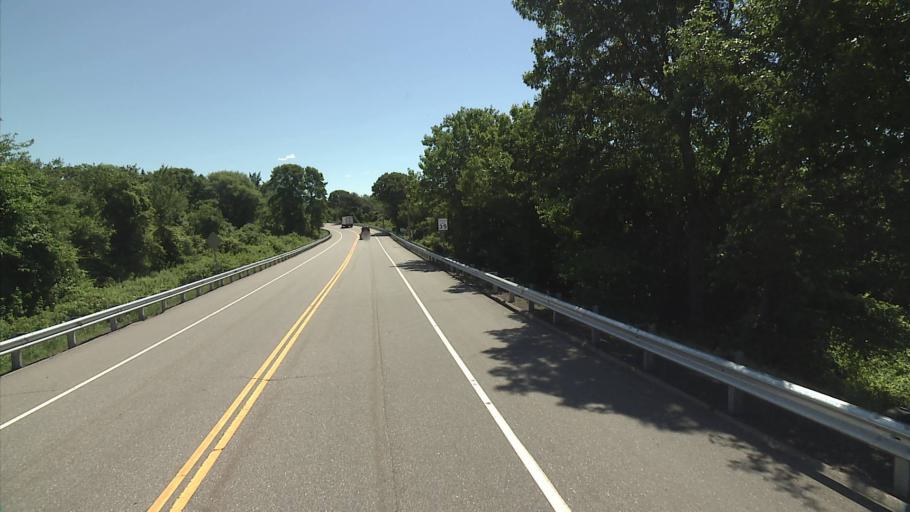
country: US
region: Connecticut
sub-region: New London County
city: Noank
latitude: 41.3238
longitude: -71.9976
